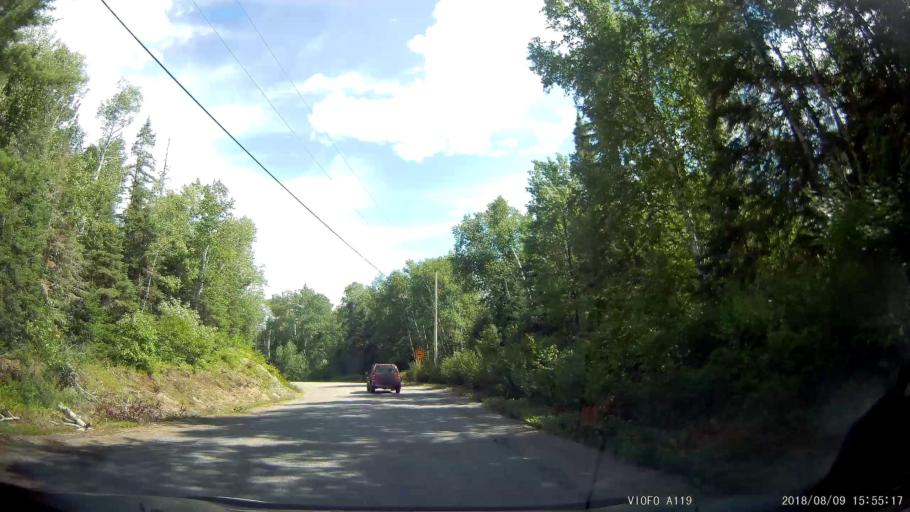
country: CA
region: Ontario
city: Rayside-Balfour
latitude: 46.6038
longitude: -81.5254
